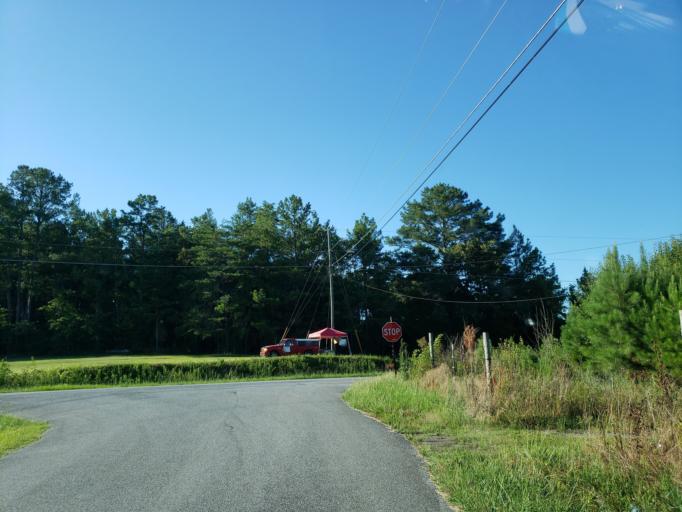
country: US
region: Georgia
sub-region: Bartow County
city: Euharlee
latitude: 34.1255
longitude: -85.0013
